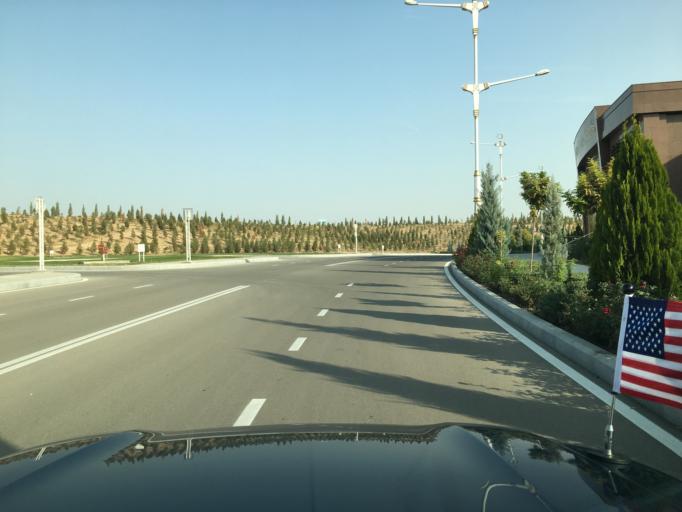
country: TM
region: Ahal
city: Ashgabat
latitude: 37.9371
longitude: 58.3114
